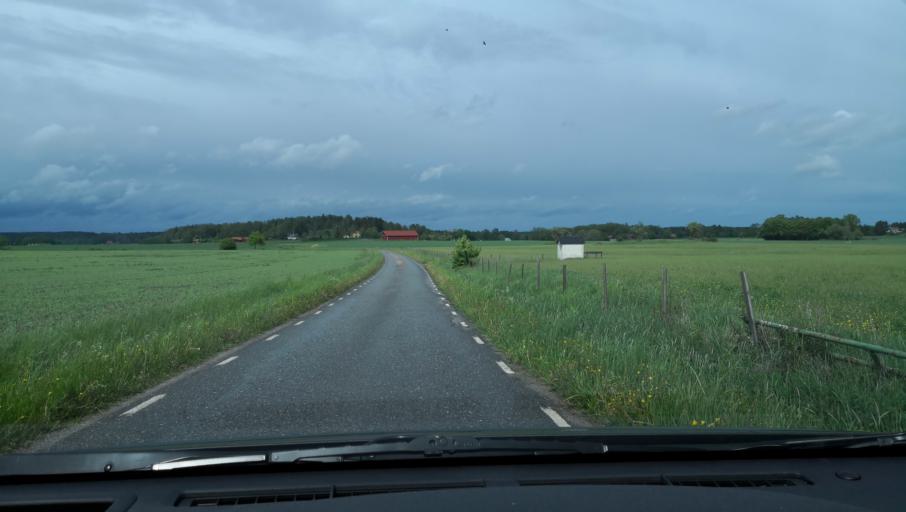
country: SE
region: Uppsala
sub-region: Enkopings Kommun
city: Orsundsbro
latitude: 59.7127
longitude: 17.4227
